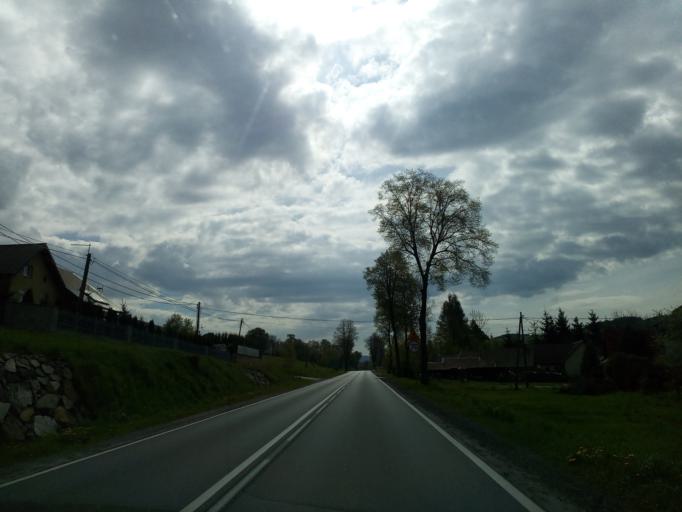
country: PL
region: Lesser Poland Voivodeship
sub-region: Powiat nowosadecki
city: Kamionka Wielka
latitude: 49.5441
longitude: 20.7863
